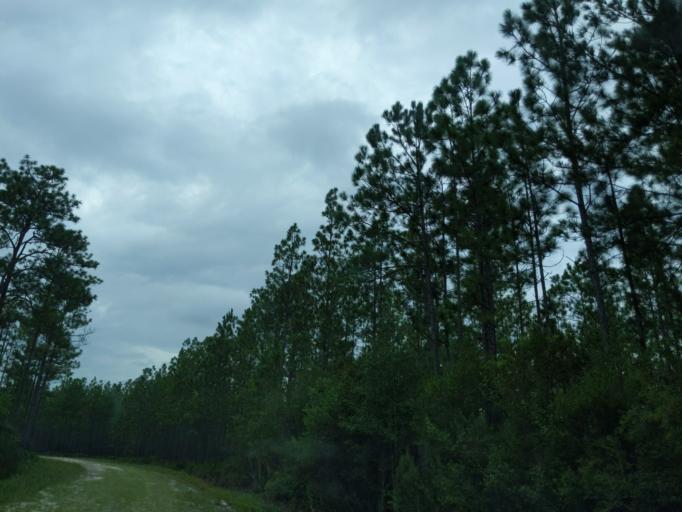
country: US
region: Florida
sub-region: Gadsden County
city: Midway
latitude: 30.3588
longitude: -84.4969
